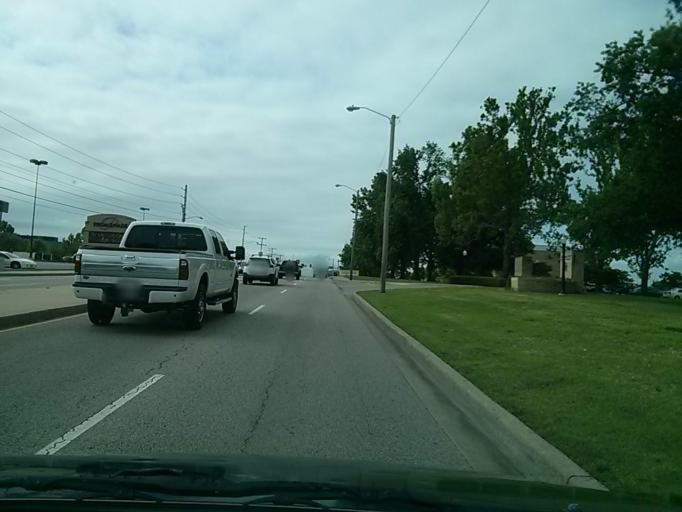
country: US
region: Oklahoma
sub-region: Tulsa County
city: Tulsa
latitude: 36.1030
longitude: -95.9224
